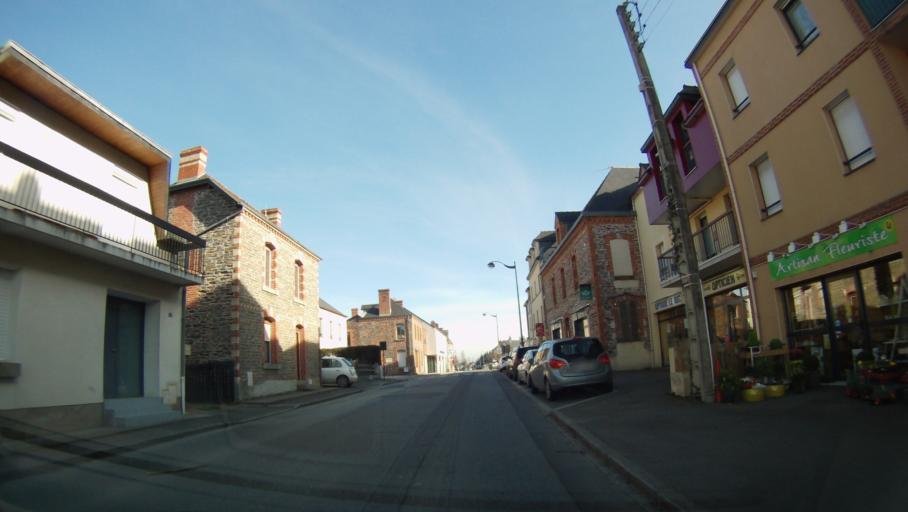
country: FR
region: Brittany
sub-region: Departement d'Ille-et-Vilaine
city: Chatillon-sur-Seiche
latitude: 48.0411
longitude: -1.6673
